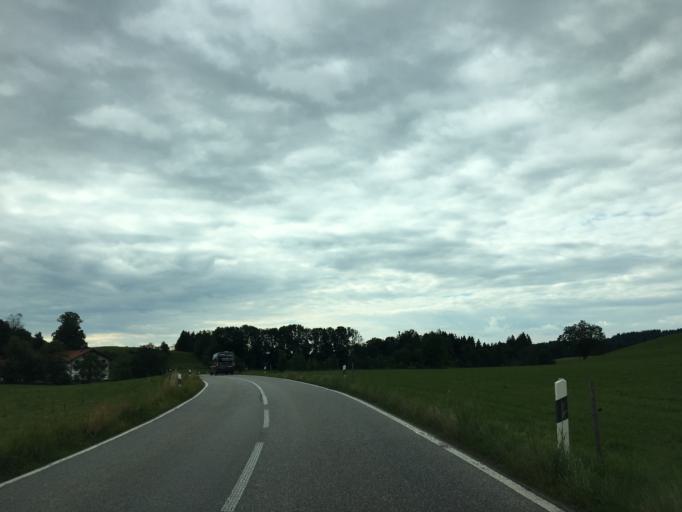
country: DE
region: Bavaria
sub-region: Upper Bavaria
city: Fischbachau
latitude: 47.7604
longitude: 11.9346
